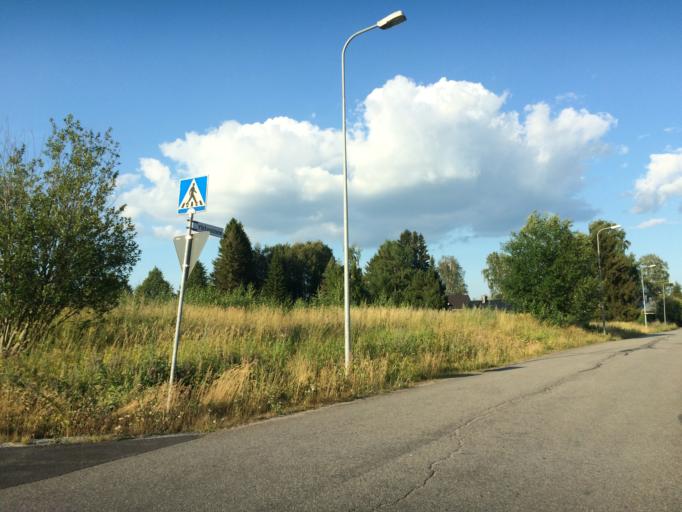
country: FI
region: Haeme
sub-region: Haemeenlinna
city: Parola
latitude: 61.0450
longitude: 24.3774
